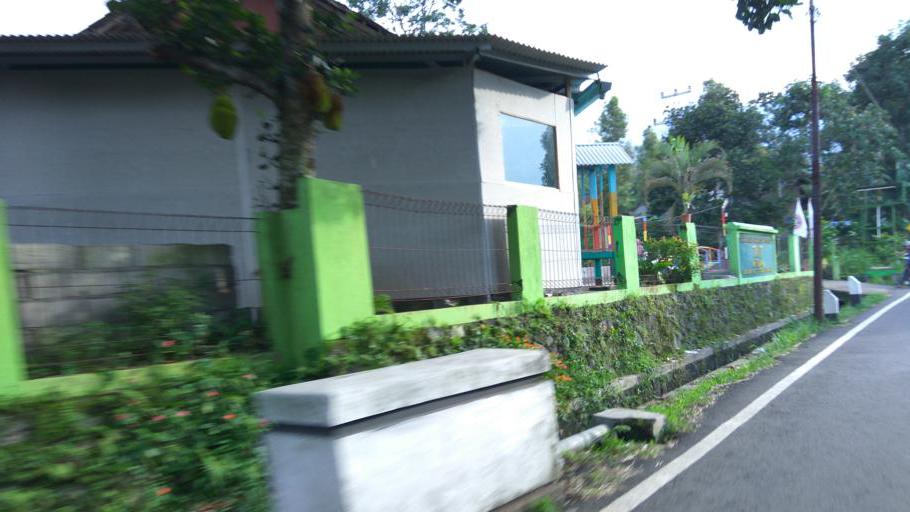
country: ID
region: Central Java
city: Salatiga
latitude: -7.3638
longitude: 110.4739
